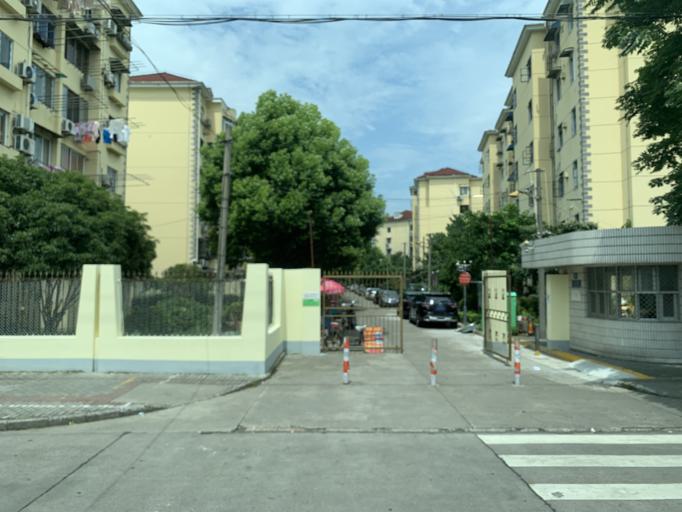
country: CN
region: Shanghai Shi
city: Huamu
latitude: 31.2486
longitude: 121.5760
